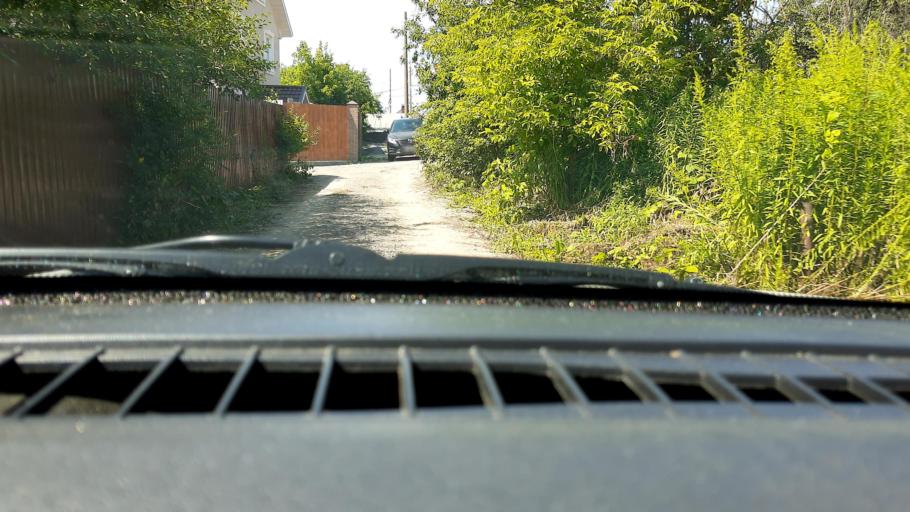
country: RU
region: Nizjnij Novgorod
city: Afonino
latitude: 56.3038
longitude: 44.0618
